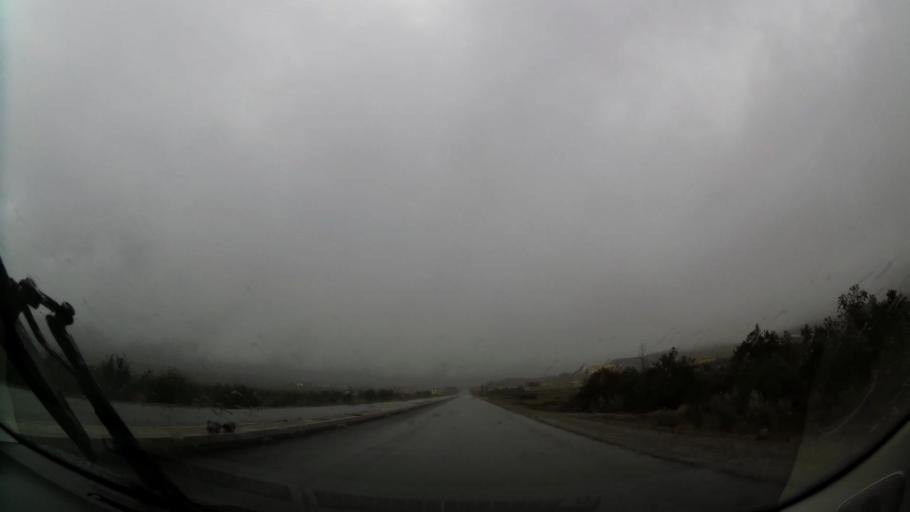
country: MA
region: Oriental
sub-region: Nador
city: Midar
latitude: 34.8426
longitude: -3.7210
